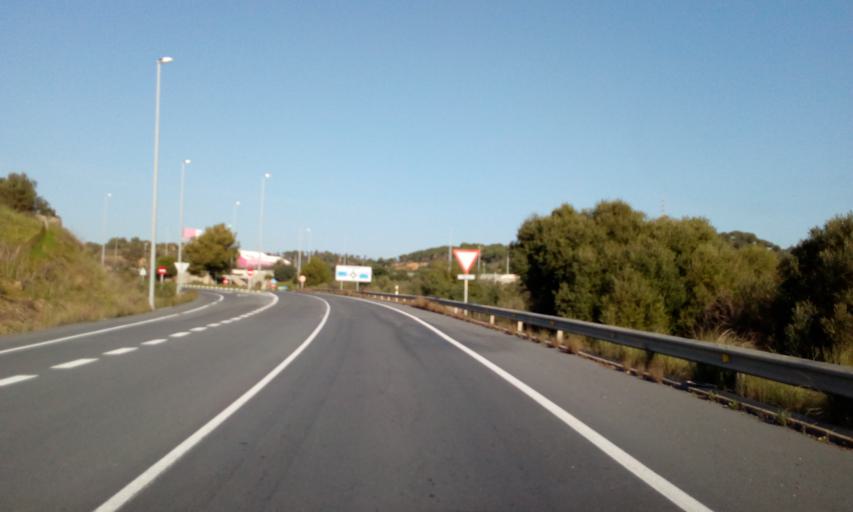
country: ES
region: Andalusia
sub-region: Provincia de Huelva
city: Ayamonte
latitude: 37.2368
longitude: -7.4040
